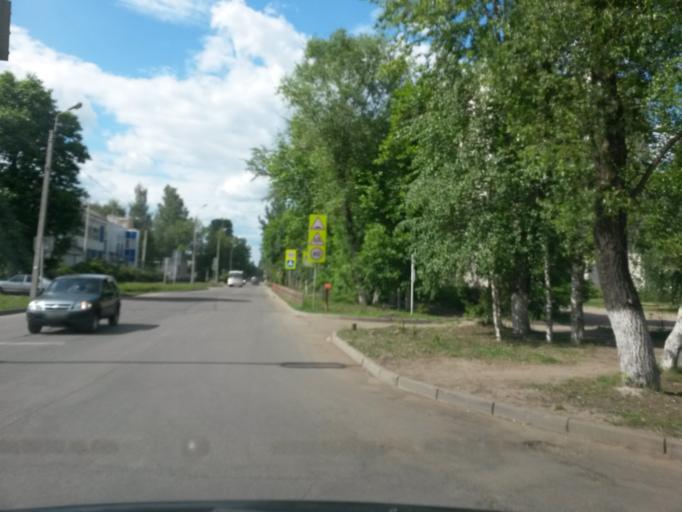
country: RU
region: Jaroslavl
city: Yaroslavl
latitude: 57.6471
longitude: 39.9399
